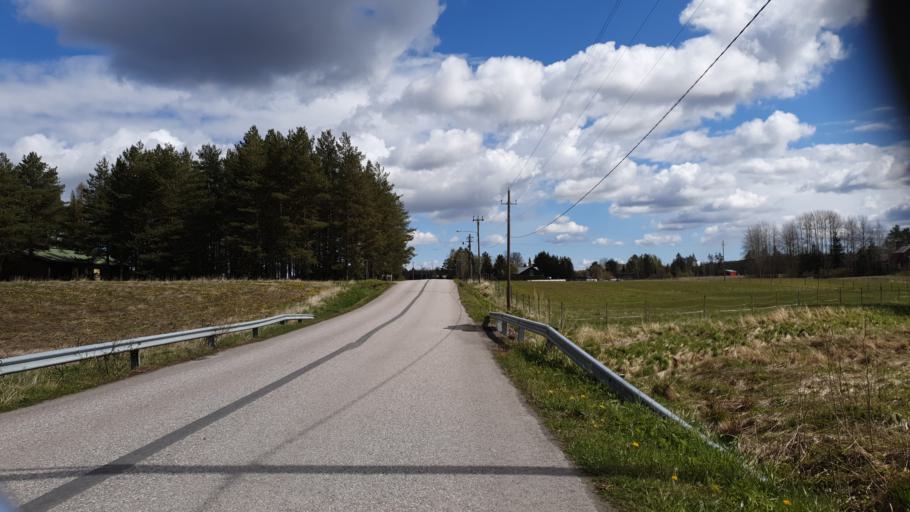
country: FI
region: Uusimaa
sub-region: Helsinki
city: Tuusula
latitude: 60.3909
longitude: 24.9097
